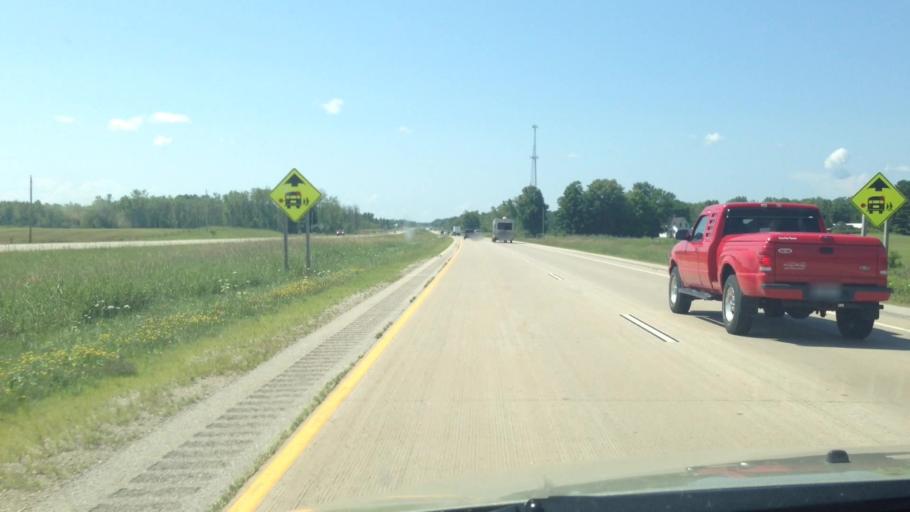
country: US
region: Wisconsin
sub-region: Marinette County
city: Peshtigo
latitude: 45.0043
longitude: -87.8495
